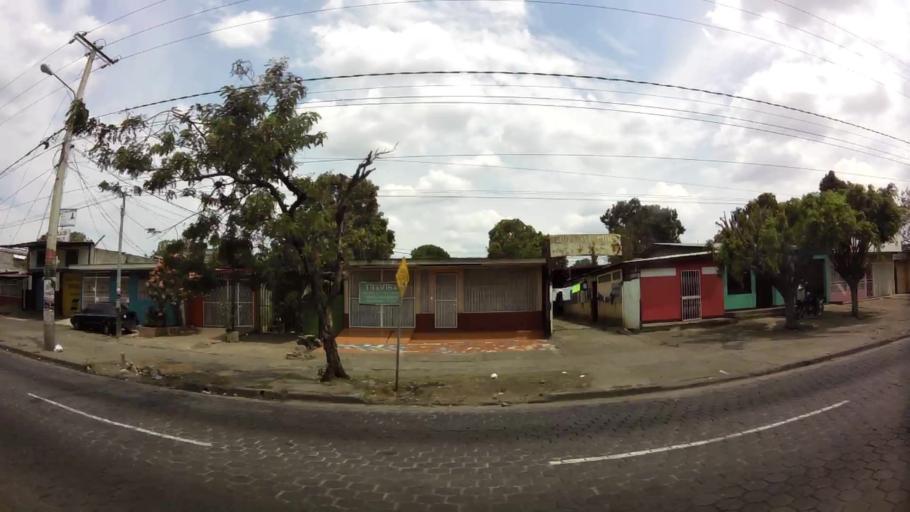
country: NI
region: Managua
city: Managua
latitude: 12.1389
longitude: -86.2479
